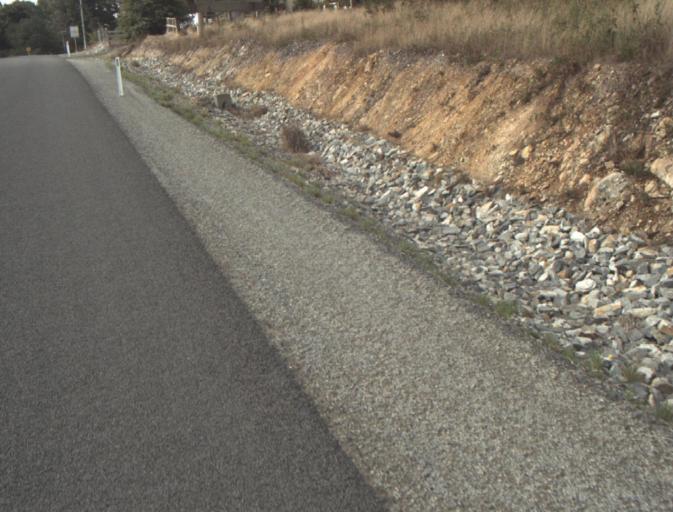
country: AU
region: Tasmania
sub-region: Launceston
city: Mayfield
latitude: -41.1946
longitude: 147.1816
